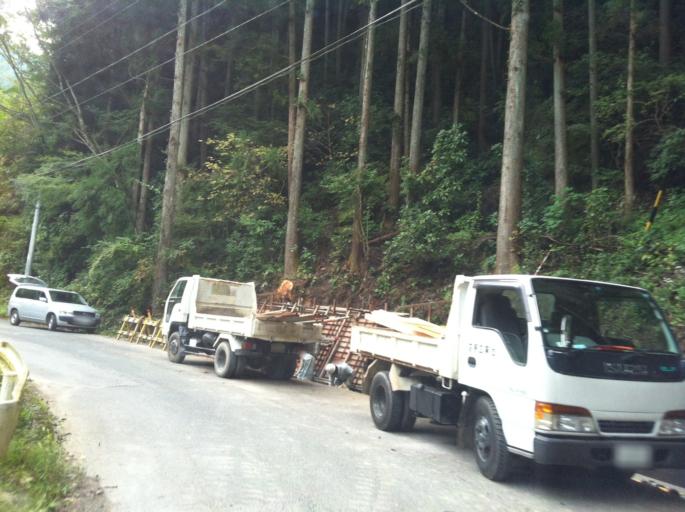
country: JP
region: Shizuoka
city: Mori
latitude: 34.8795
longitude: 138.0274
